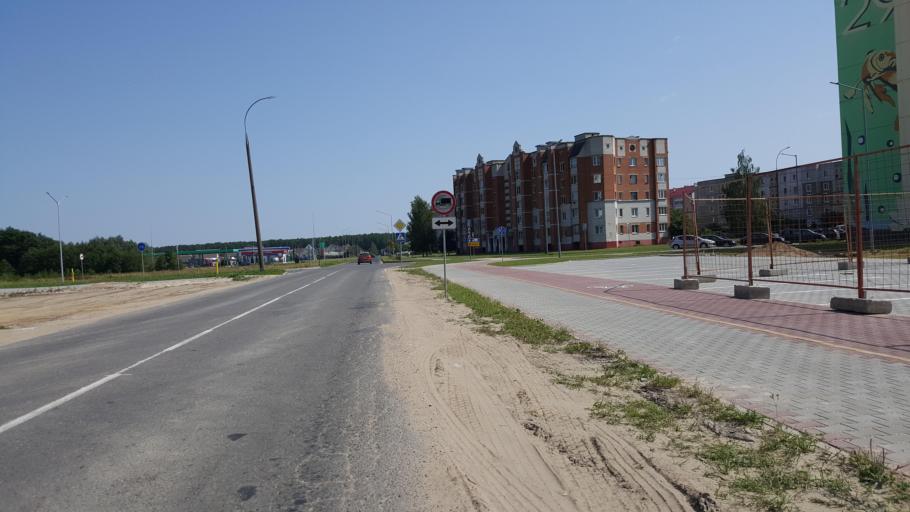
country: BY
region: Brest
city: Zhabinka
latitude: 52.1964
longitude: 24.0338
